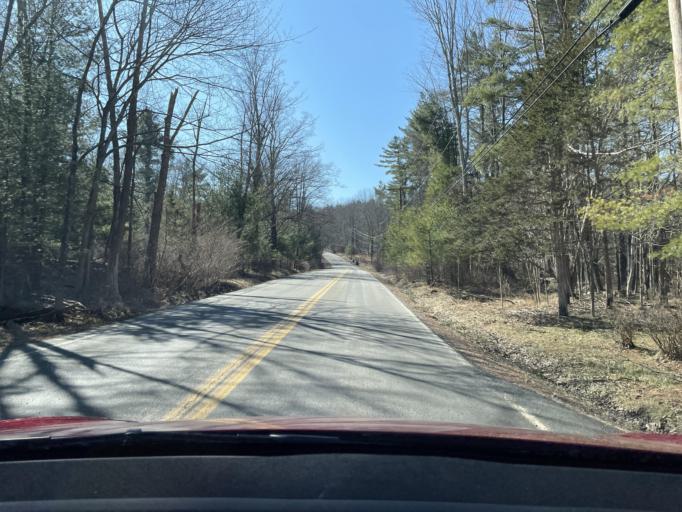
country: US
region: New York
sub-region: Ulster County
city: Woodstock
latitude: 42.0310
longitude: -74.1247
